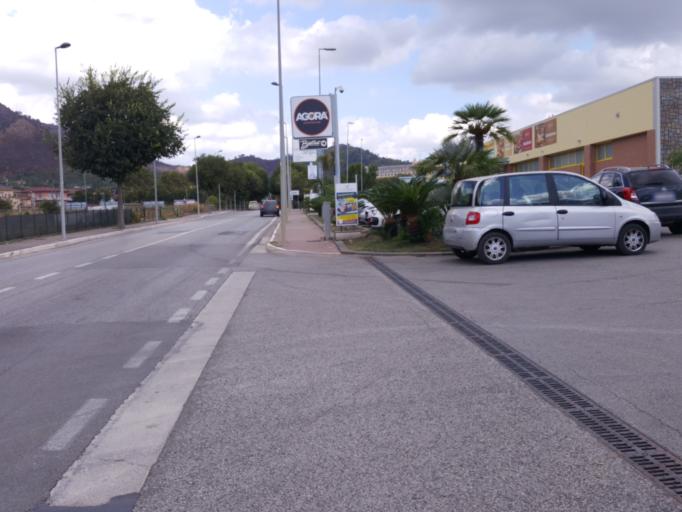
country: IT
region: Campania
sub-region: Provincia di Salerno
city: Baronissi
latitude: 40.7429
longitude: 14.7747
